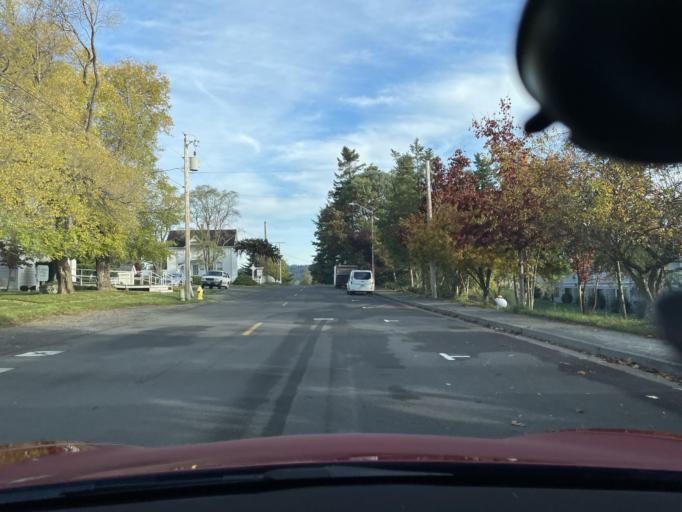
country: US
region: Washington
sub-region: San Juan County
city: Friday Harbor
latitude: 48.5319
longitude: -123.0244
